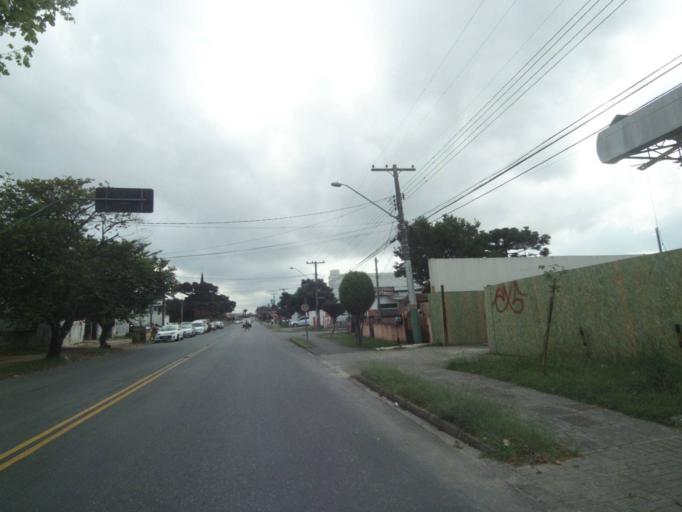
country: BR
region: Parana
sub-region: Pinhais
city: Pinhais
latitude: -25.4496
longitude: -49.2047
